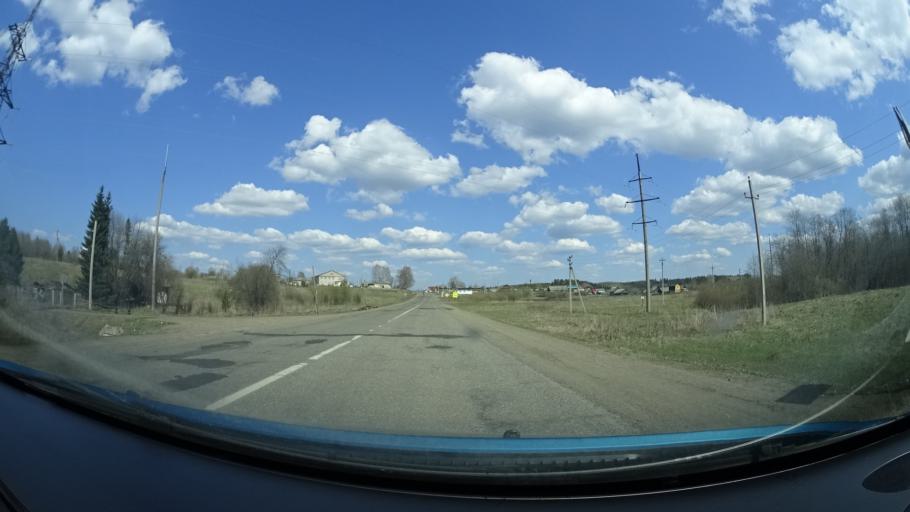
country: RU
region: Perm
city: Osa
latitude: 57.4507
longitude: 55.6542
